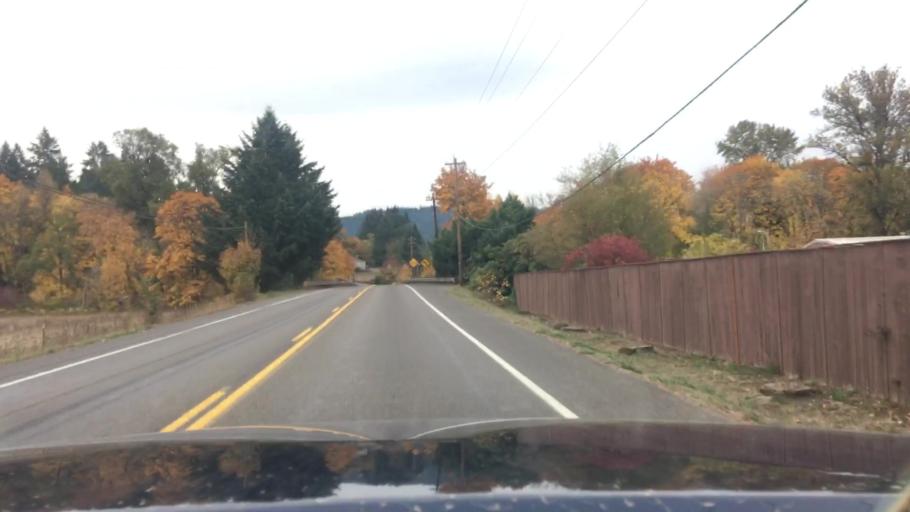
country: US
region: Oregon
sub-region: Lane County
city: Cottage Grove
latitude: 43.7646
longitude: -123.0654
